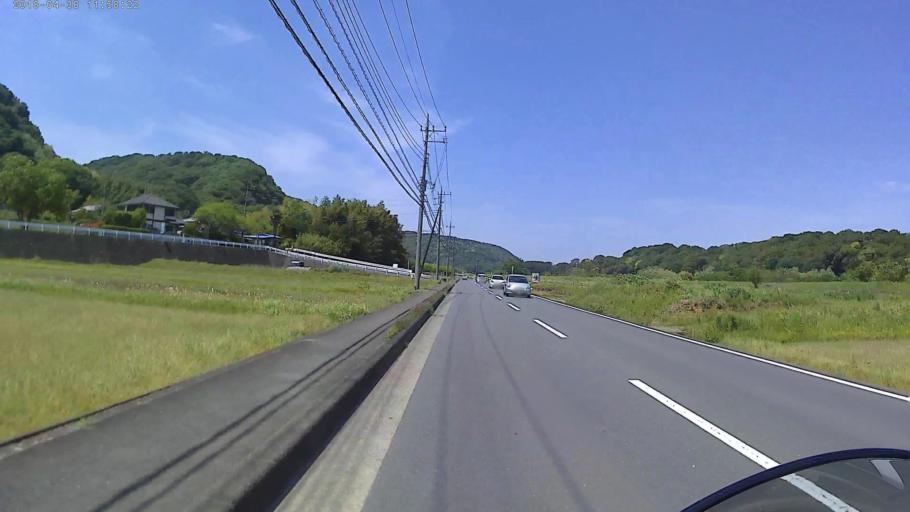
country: JP
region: Kanagawa
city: Zama
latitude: 35.5010
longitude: 139.3366
